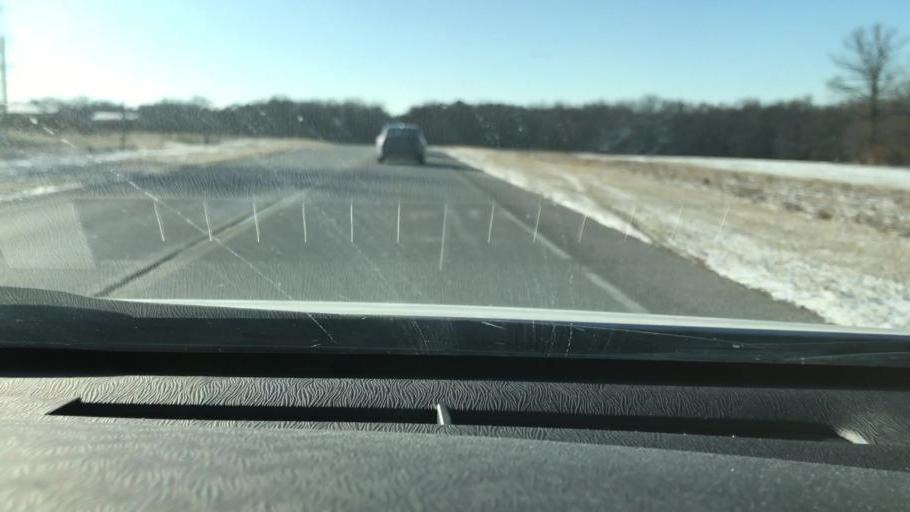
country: US
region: Maryland
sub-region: Prince George's County
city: Greenbelt
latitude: 39.0290
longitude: -76.8478
